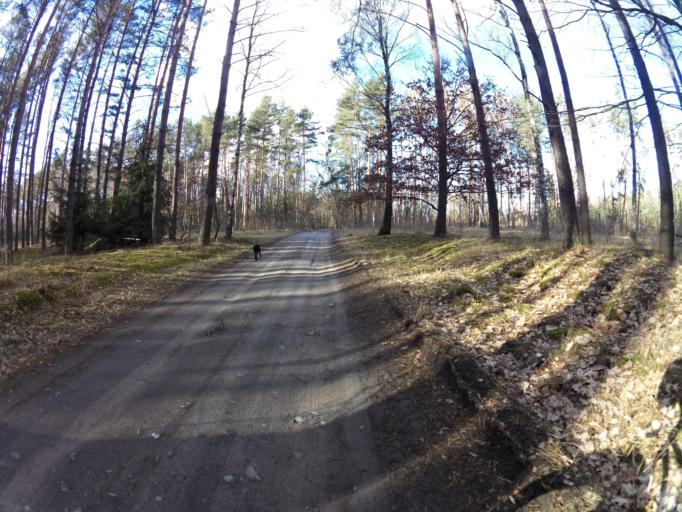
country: PL
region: West Pomeranian Voivodeship
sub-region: Powiat mysliborski
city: Debno
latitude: 52.8008
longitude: 14.7479
